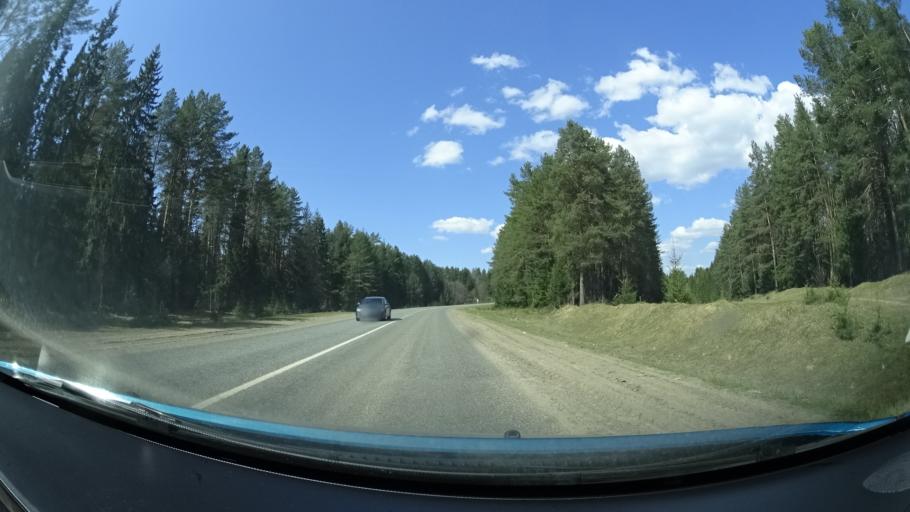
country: RU
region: Perm
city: Yugo-Kamskiy
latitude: 57.5595
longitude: 55.6817
